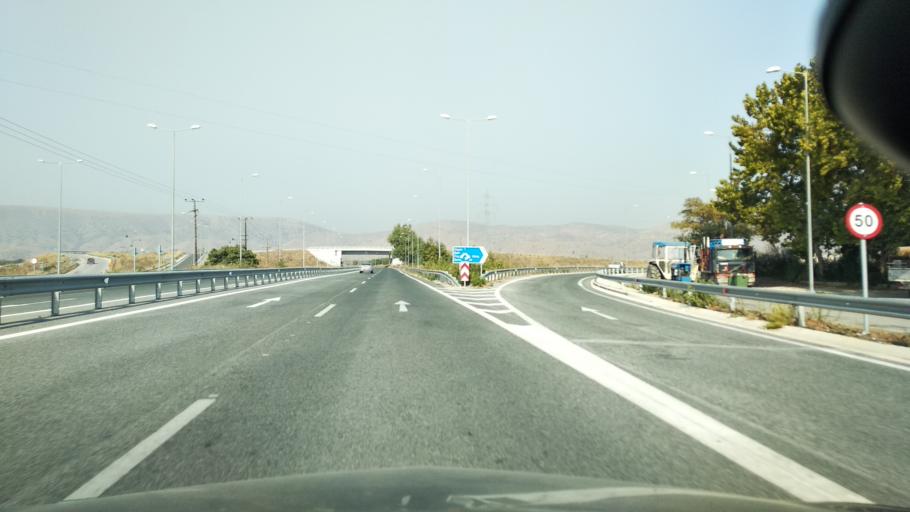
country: GR
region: Thessaly
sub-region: Trikala
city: Zarkos
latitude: 39.5919
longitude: 22.1268
